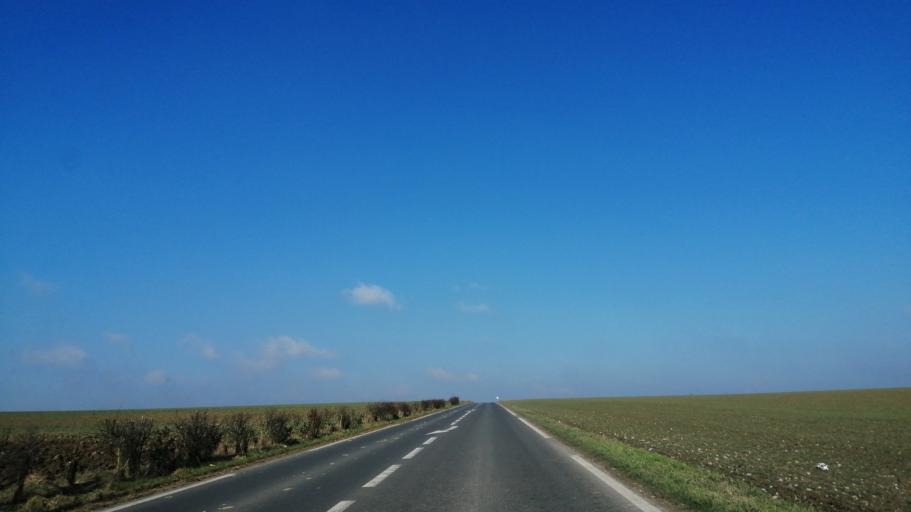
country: FR
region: Nord-Pas-de-Calais
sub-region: Departement du Pas-de-Calais
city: Ranchicourt
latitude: 50.4178
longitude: 2.5767
